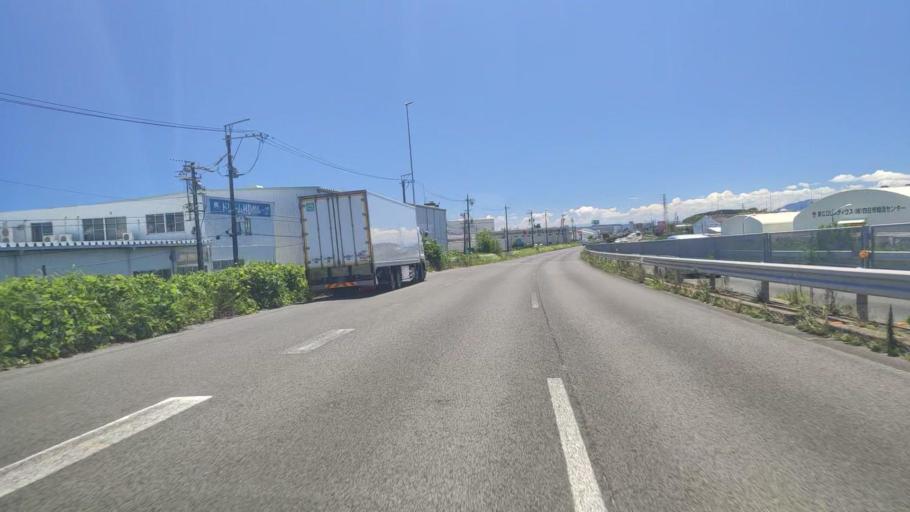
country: JP
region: Mie
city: Yokkaichi
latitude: 34.9220
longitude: 136.6136
